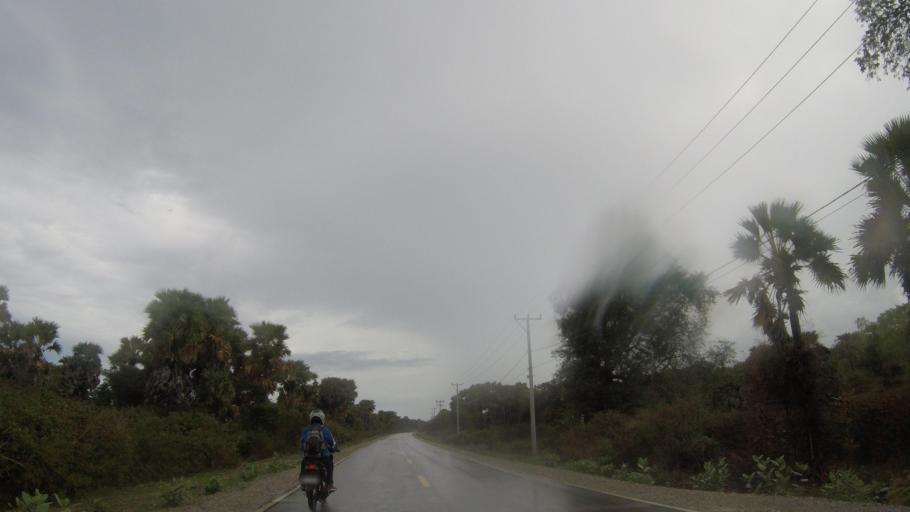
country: TL
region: Lautem
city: Lospalos
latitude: -8.3809
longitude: 126.8627
